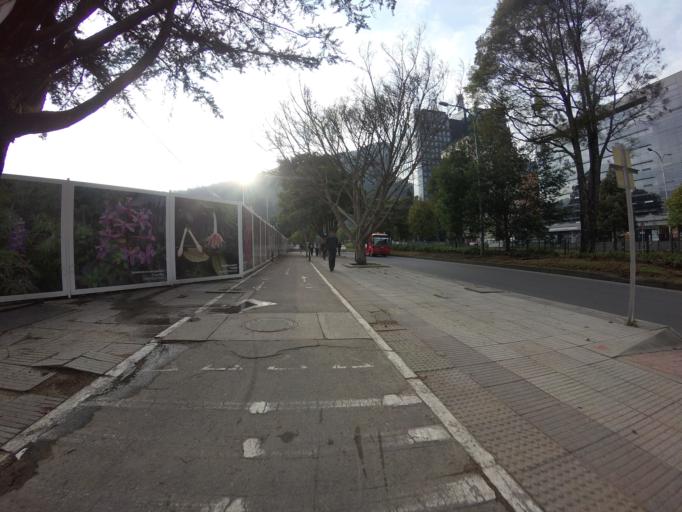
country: CO
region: Bogota D.C.
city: Barrio San Luis
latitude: 4.6811
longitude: -74.0399
